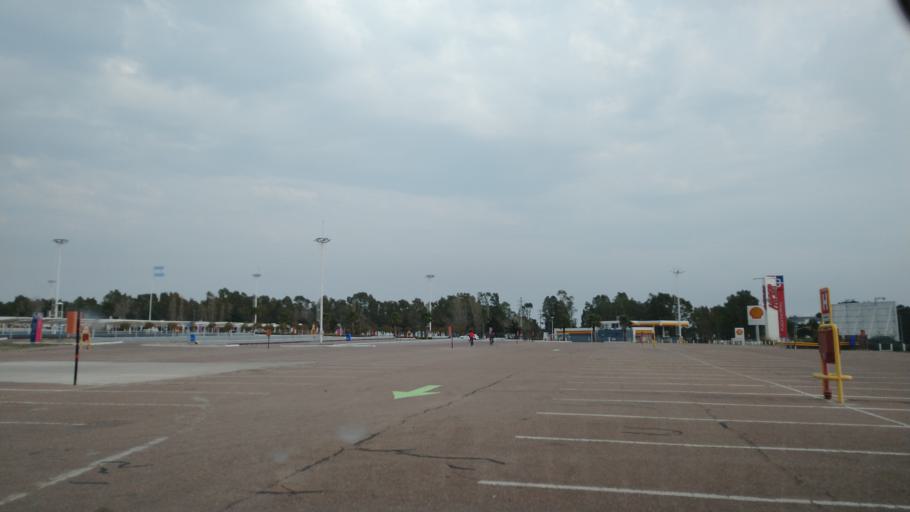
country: AR
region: Buenos Aires
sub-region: Partido de Bahia Blanca
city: Bahia Blanca
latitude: -38.6984
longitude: -62.2425
